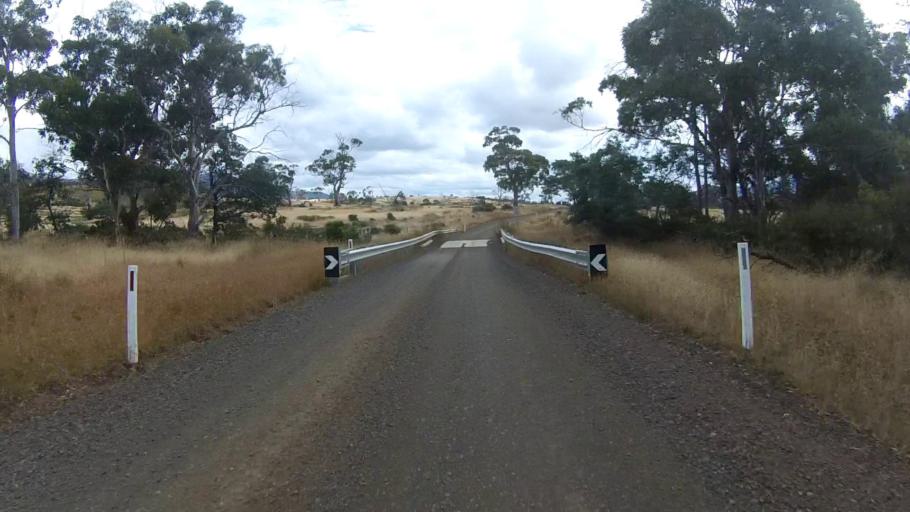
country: AU
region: Tasmania
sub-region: Break O'Day
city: St Helens
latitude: -41.8263
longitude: 147.9785
